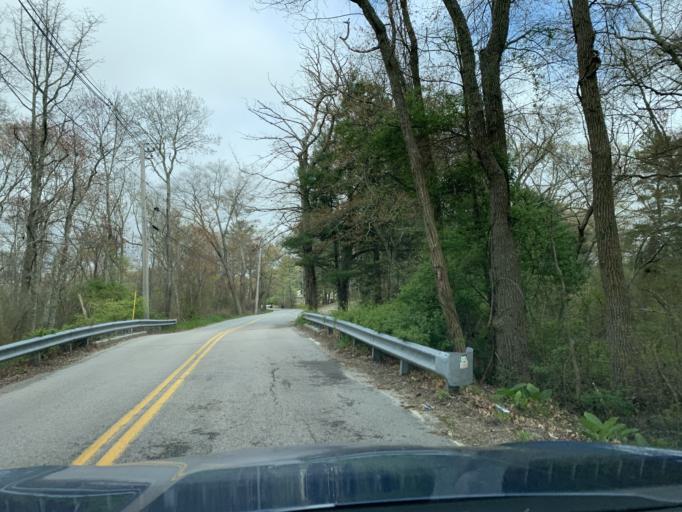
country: US
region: Rhode Island
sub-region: Washington County
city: Exeter
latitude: 41.6070
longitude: -71.4919
